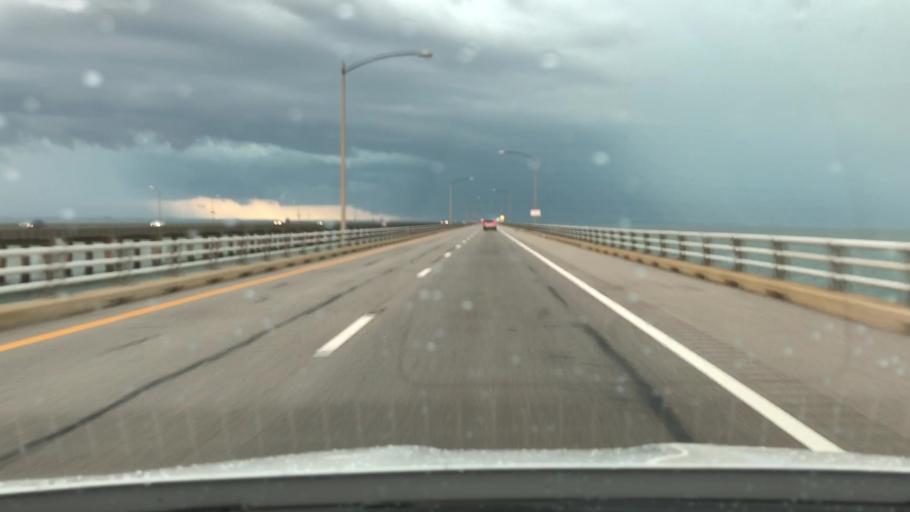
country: US
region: Virginia
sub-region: City of Virginia Beach
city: Virginia Beach
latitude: 37.0160
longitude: -76.0930
